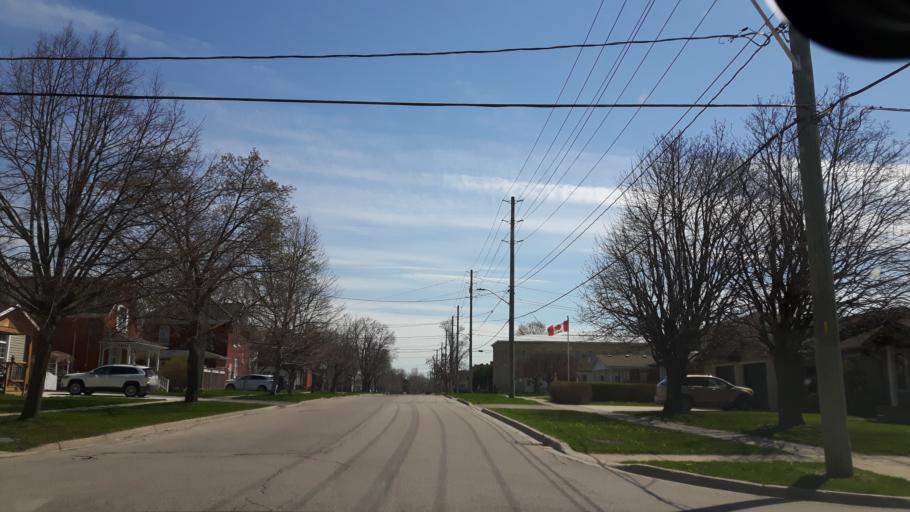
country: CA
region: Ontario
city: Goderich
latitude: 43.7441
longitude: -81.7047
